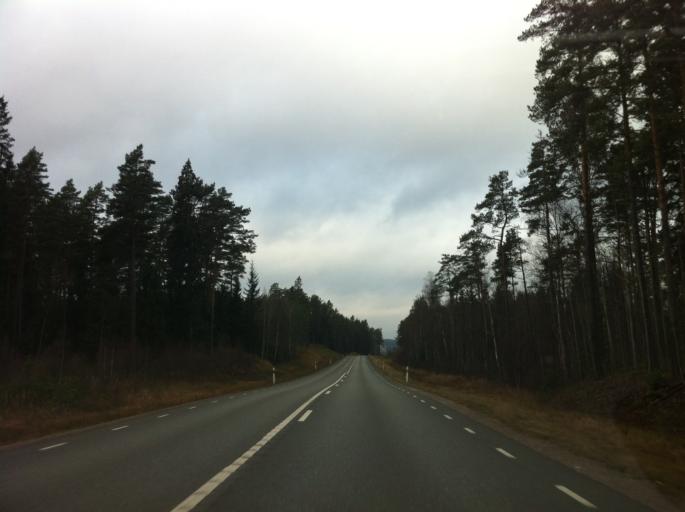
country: SE
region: Joenkoeping
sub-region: Vetlanda Kommun
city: Vetlanda
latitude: 57.4107
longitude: 15.2766
